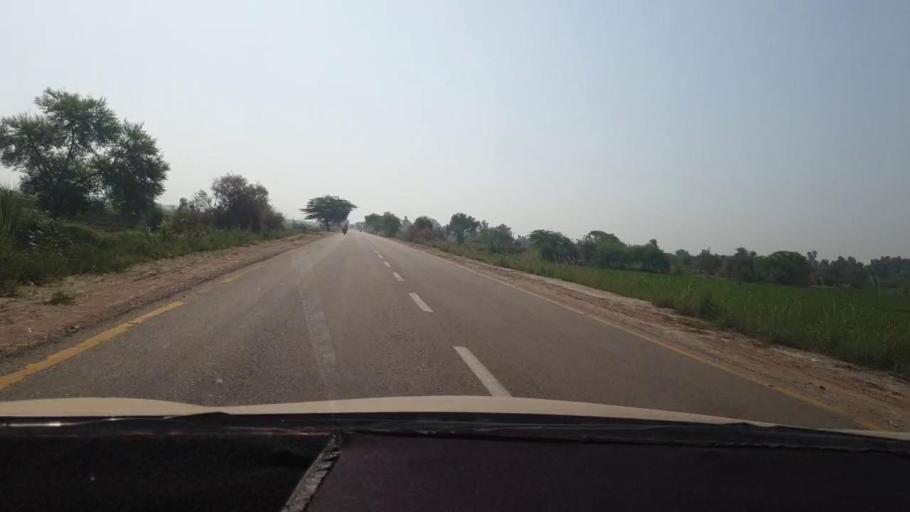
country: PK
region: Sindh
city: Miro Khan
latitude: 27.7268
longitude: 68.1351
